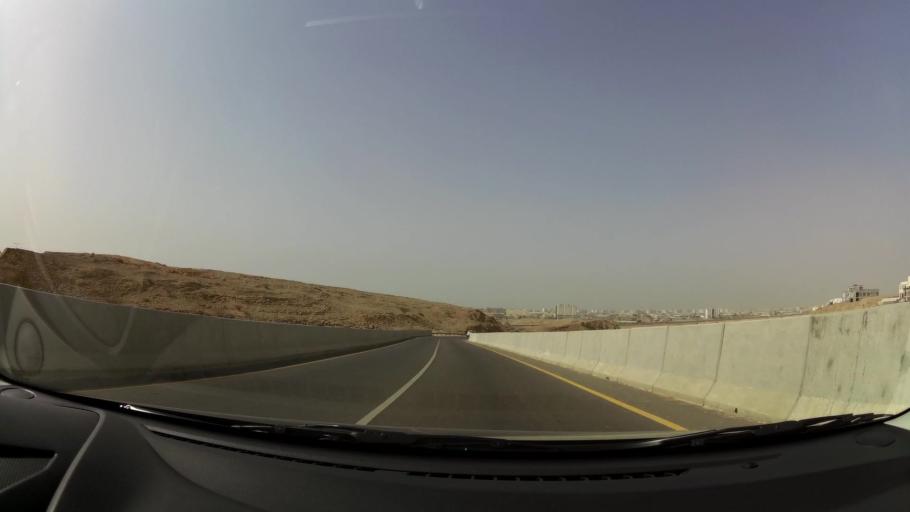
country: OM
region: Muhafazat Masqat
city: Bawshar
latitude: 23.5566
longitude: 58.3406
